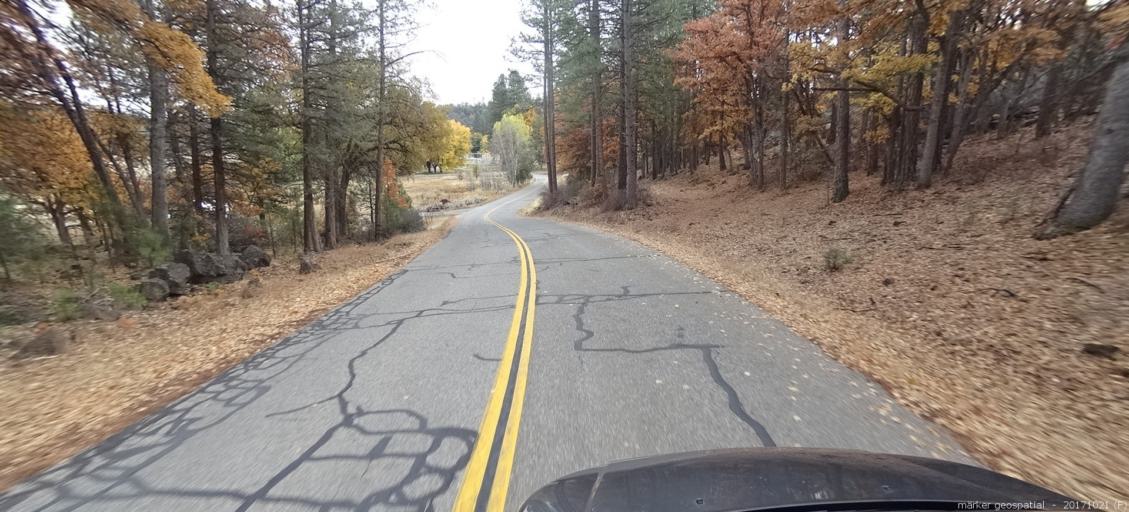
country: US
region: California
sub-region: Shasta County
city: Burney
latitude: 40.9321
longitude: -121.5491
